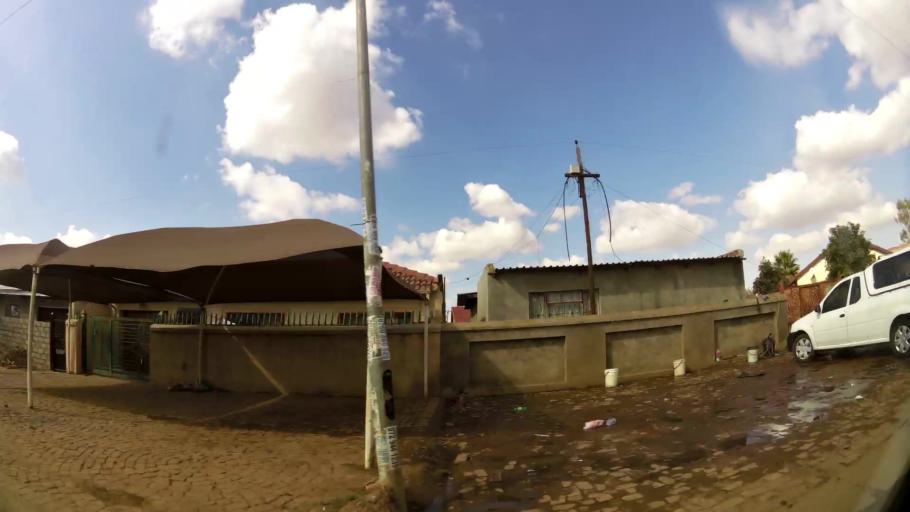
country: ZA
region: Gauteng
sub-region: City of Tshwane Metropolitan Municipality
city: Cullinan
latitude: -25.7037
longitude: 28.4134
